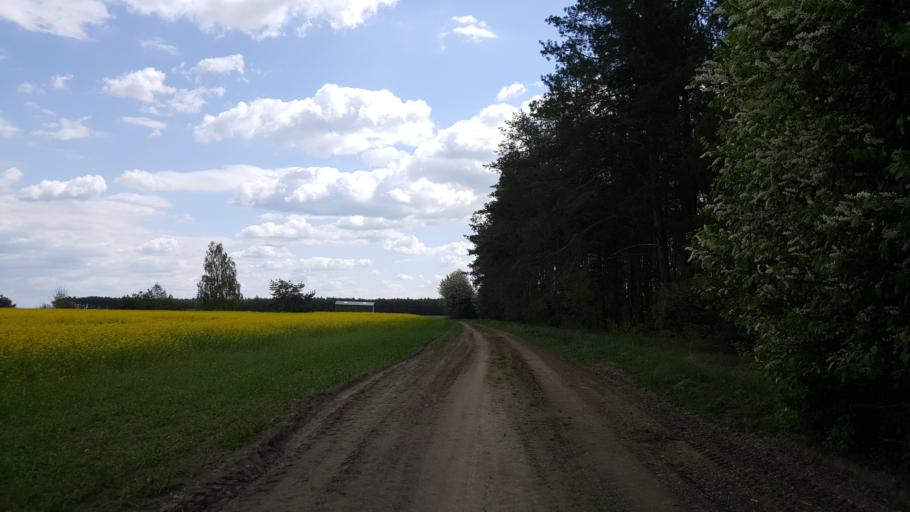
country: BY
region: Brest
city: Kamyanyets
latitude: 52.3870
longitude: 23.9431
